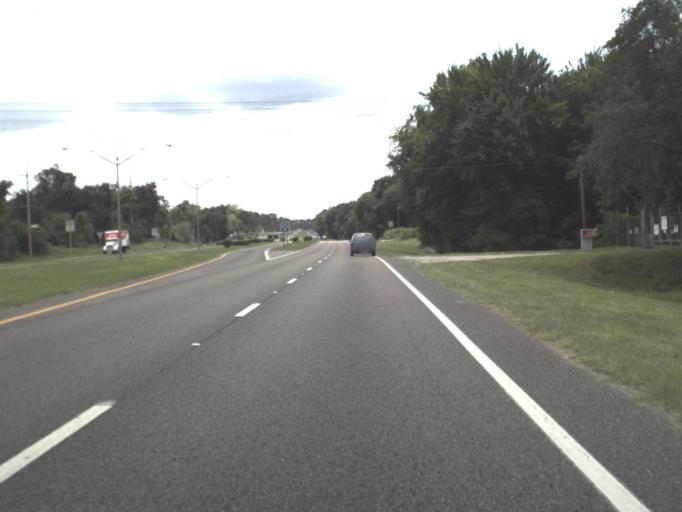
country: US
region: Florida
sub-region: Putnam County
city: East Palatka
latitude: 29.6263
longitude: -81.5872
